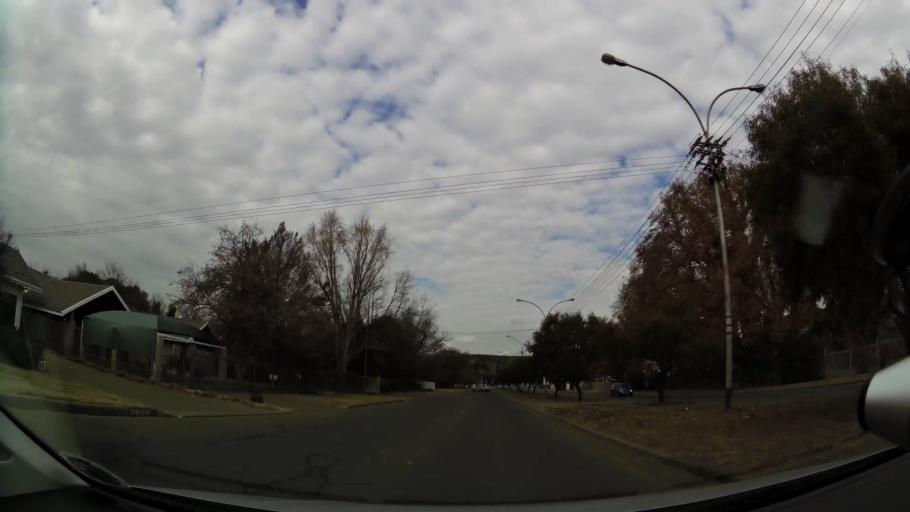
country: ZA
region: Orange Free State
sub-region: Mangaung Metropolitan Municipality
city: Bloemfontein
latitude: -29.0862
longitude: 26.2282
